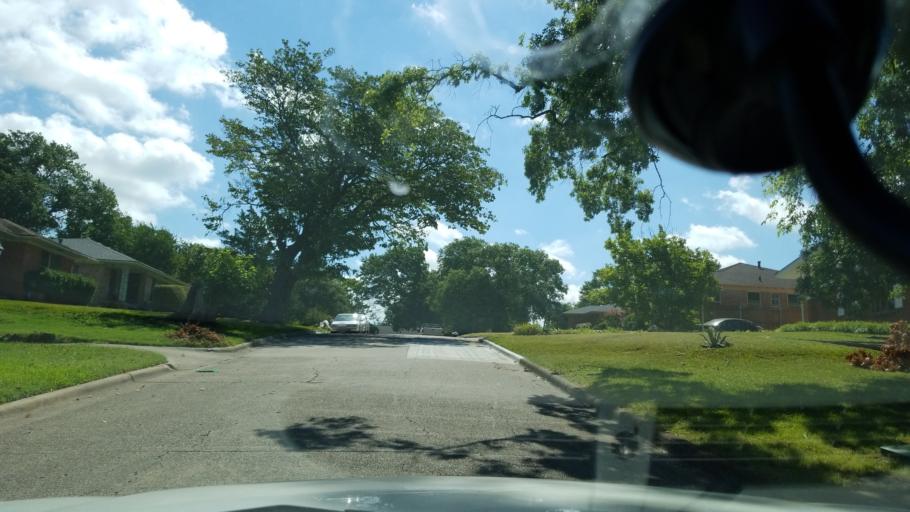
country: US
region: Texas
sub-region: Dallas County
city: Cockrell Hill
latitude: 32.6831
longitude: -96.8132
